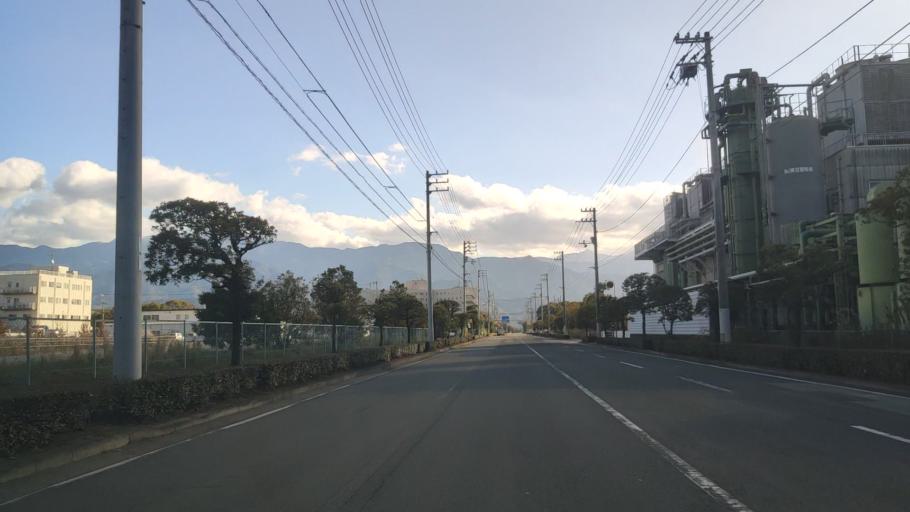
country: JP
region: Ehime
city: Saijo
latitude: 33.9384
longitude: 133.1918
